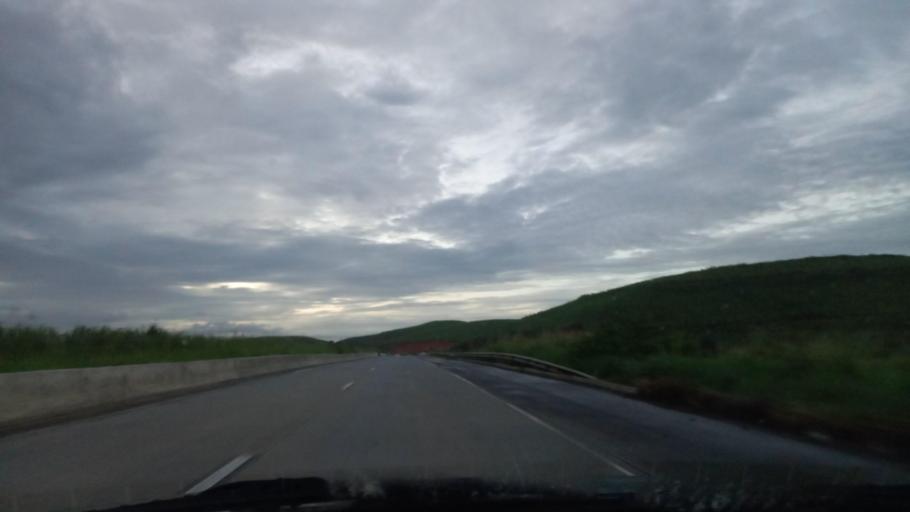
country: BR
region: Pernambuco
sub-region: Ribeirao
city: Ribeirao
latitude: -8.5233
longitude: -35.3897
